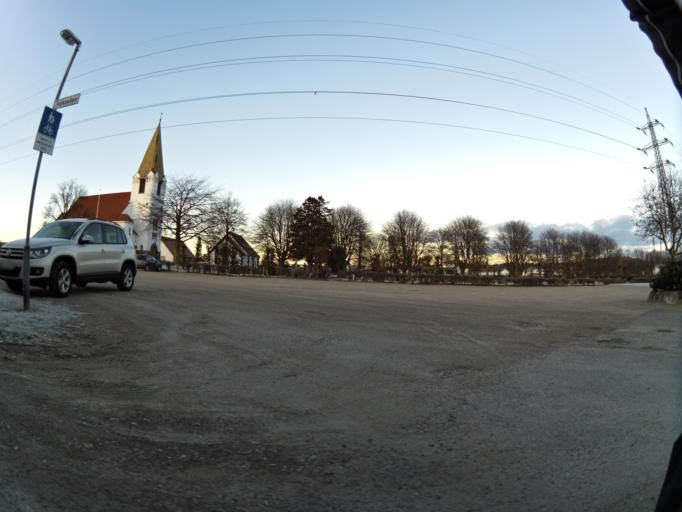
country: NO
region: Ostfold
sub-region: Sarpsborg
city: Sarpsborg
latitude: 59.2654
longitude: 11.0178
